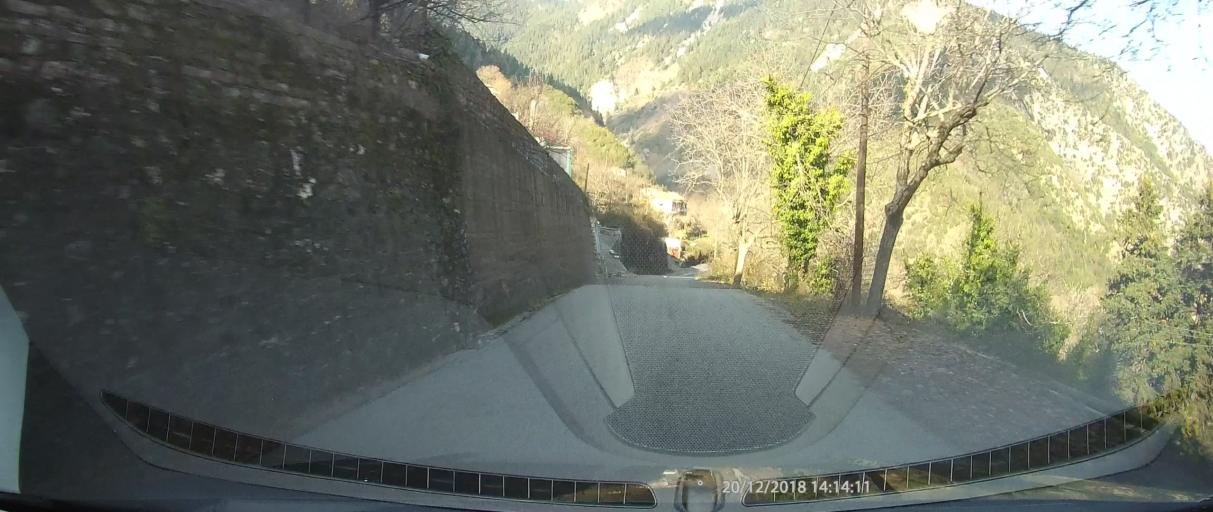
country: GR
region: West Greece
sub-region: Nomos Aitolias kai Akarnanias
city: Thermo
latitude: 38.7456
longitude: 21.6529
